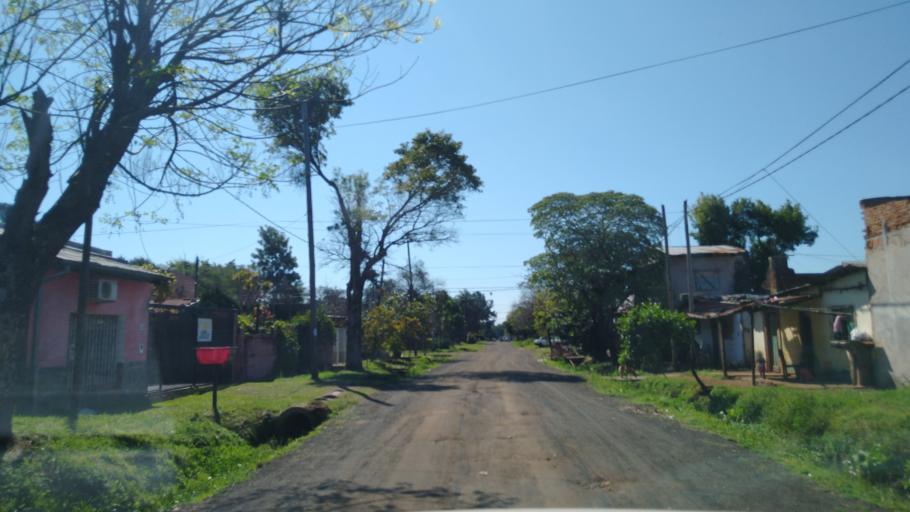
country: AR
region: Misiones
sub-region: Departamento de Capital
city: Posadas
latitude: -27.3808
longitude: -55.9213
